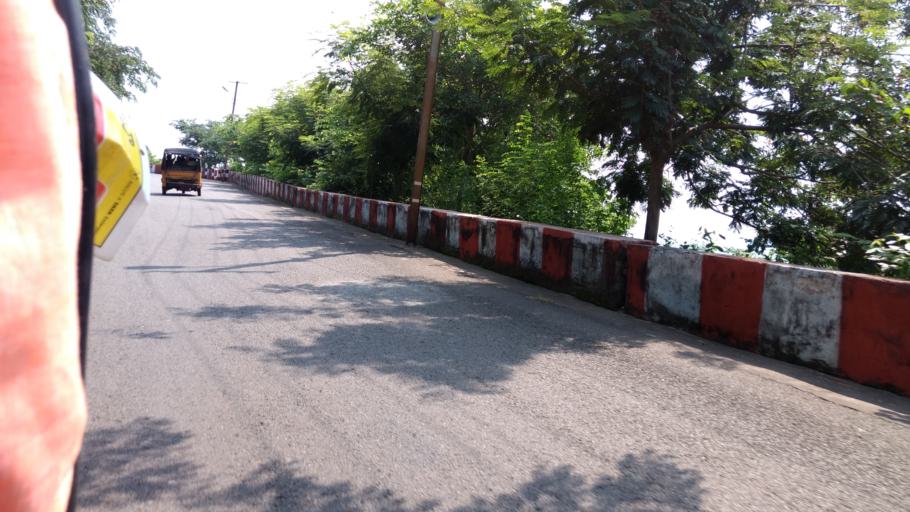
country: IN
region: Andhra Pradesh
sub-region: East Godavari
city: Tuni
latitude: 17.2806
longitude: 82.3991
